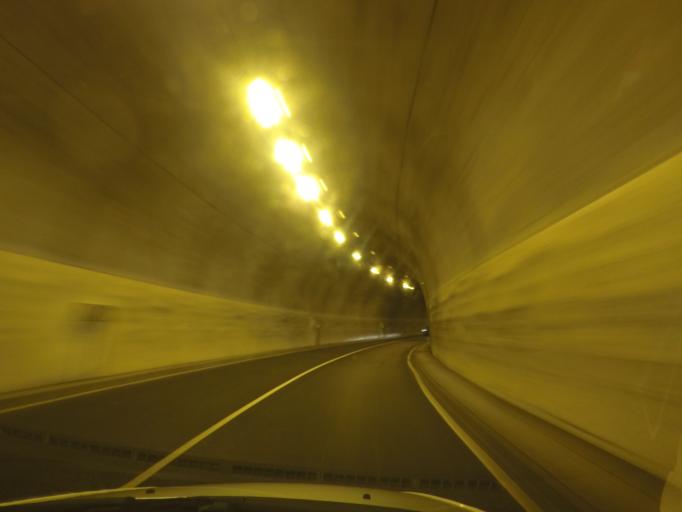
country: PT
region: Madeira
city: Ribeira Brava
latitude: 32.6741
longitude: -17.0618
